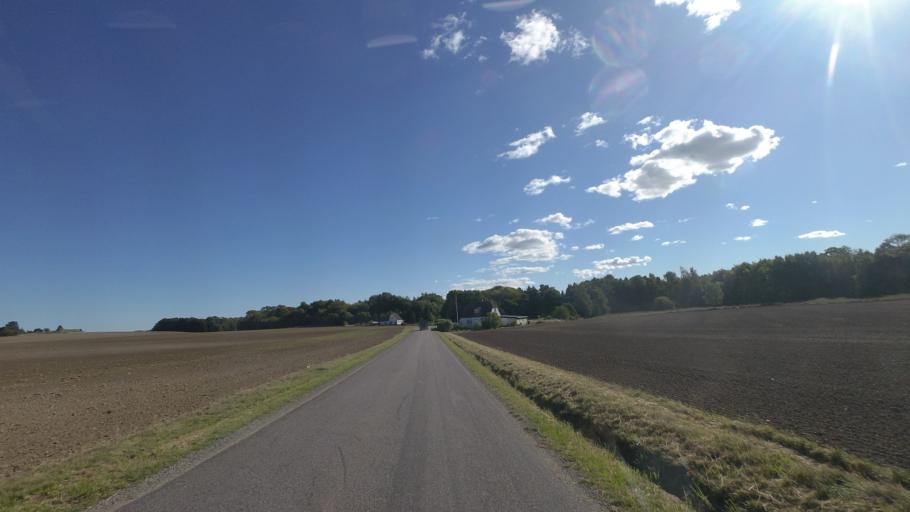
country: DK
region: Capital Region
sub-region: Bornholm Kommune
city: Akirkeby
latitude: 55.1345
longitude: 15.0198
